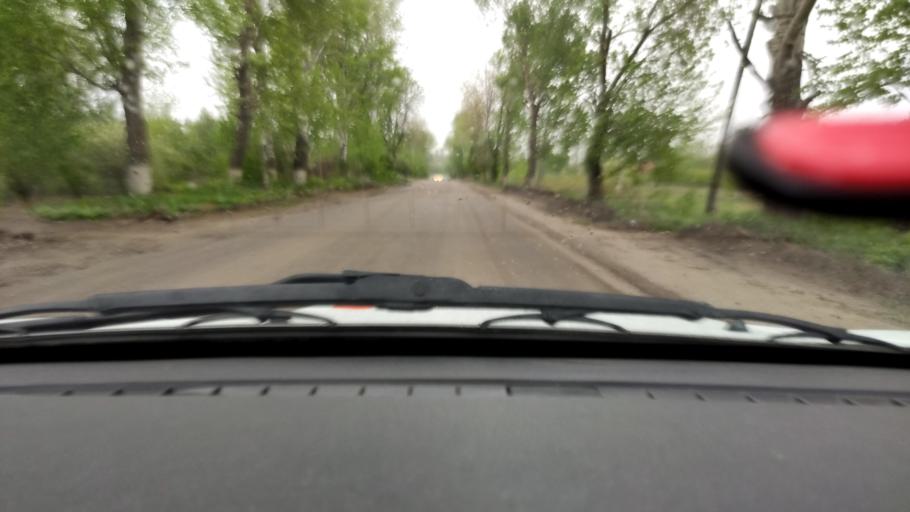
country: RU
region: Voronezj
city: Strelitsa
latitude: 51.6063
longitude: 38.9009
